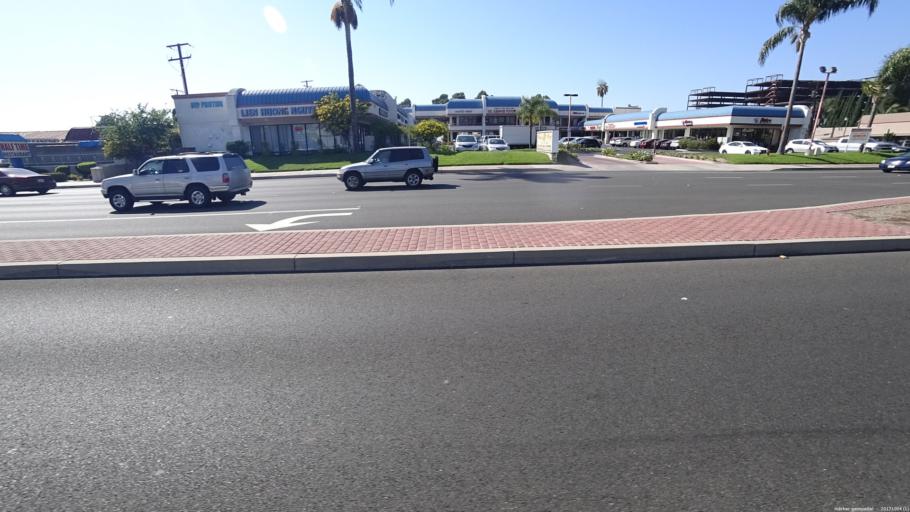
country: US
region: California
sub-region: Orange County
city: Garden Grove
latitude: 33.7716
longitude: -117.9549
